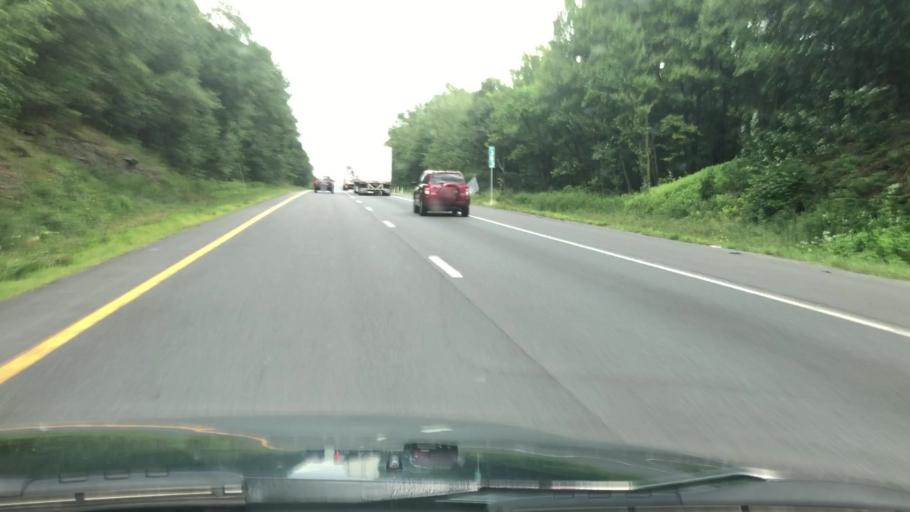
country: US
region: Pennsylvania
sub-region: Pike County
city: Conashaugh Lakes
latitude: 41.3478
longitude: -74.9859
